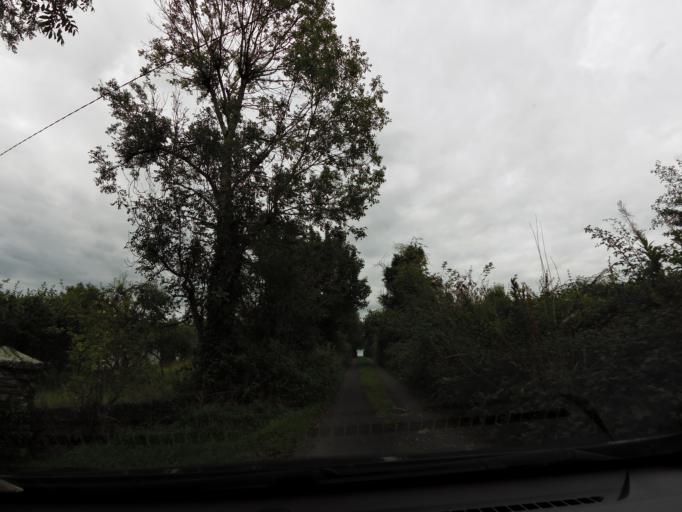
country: IE
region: Connaught
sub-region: County Galway
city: Loughrea
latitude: 53.1586
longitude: -8.4544
